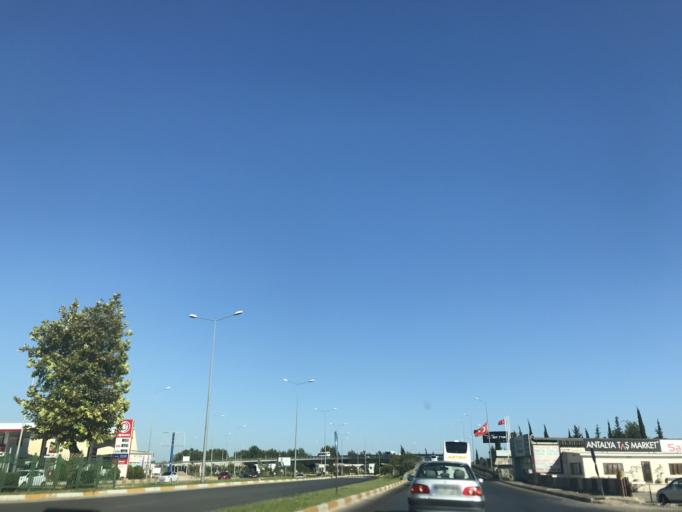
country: TR
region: Antalya
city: Antalya
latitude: 36.9011
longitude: 30.7602
